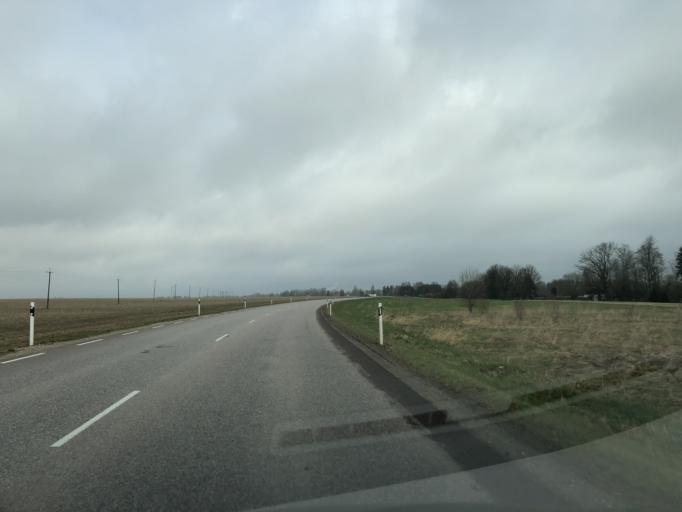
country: EE
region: Jogevamaa
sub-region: Jogeva linn
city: Jogeva
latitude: 58.7161
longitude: 26.3982
